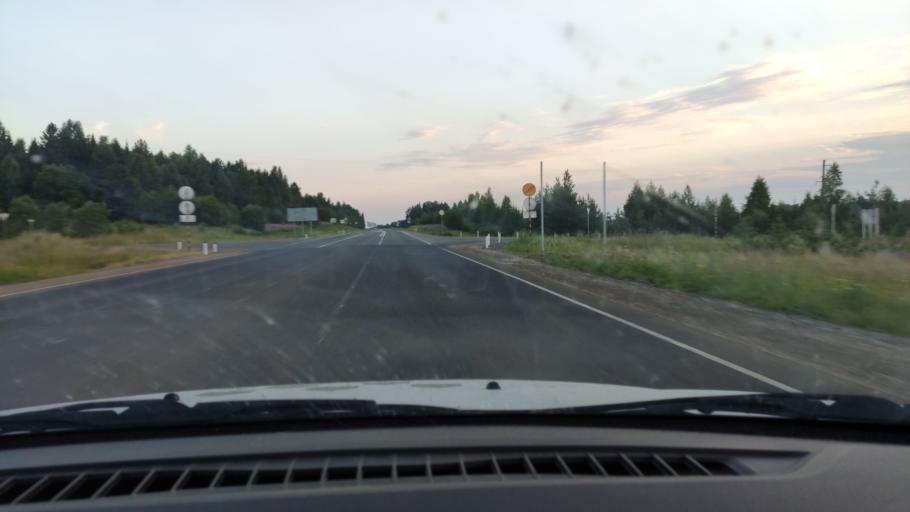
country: RU
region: Perm
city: Siva
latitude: 58.4269
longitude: 54.4506
